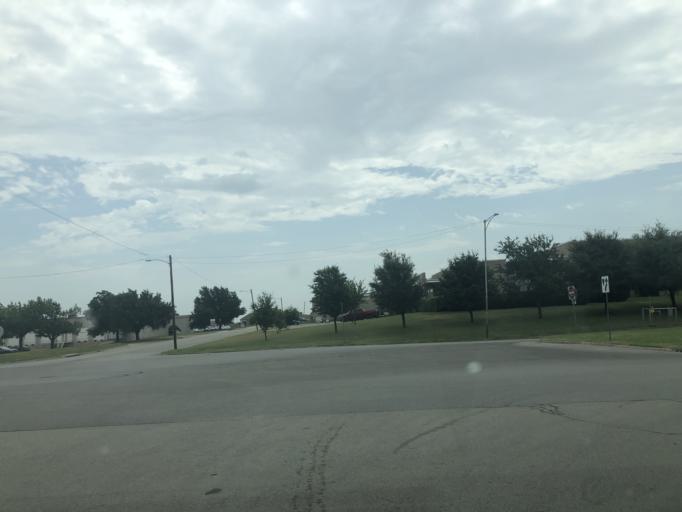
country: US
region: Texas
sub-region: Dallas County
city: Grand Prairie
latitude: 32.7670
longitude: -97.0460
